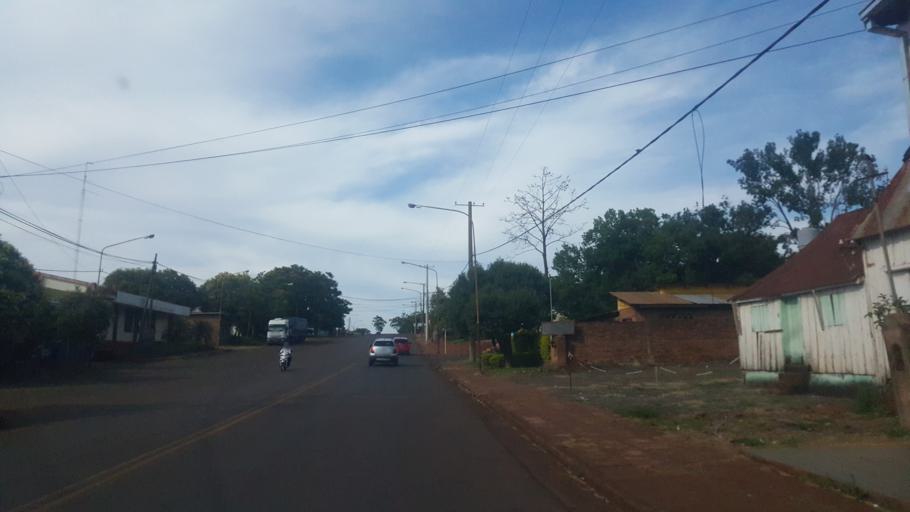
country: AR
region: Misiones
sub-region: Departamento de Leandro N. Alem
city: Leandro N. Alem
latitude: -27.5973
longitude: -55.3243
